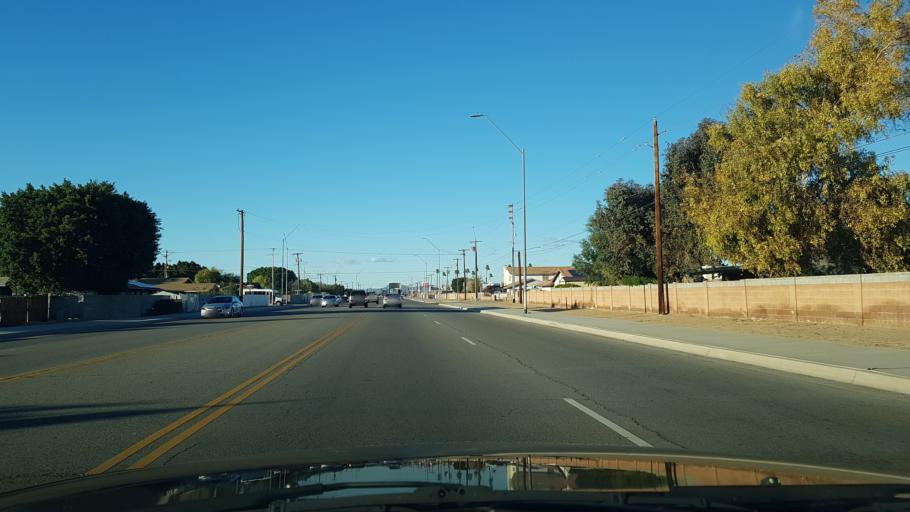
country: US
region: Arizona
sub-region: Yuma County
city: Yuma
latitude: 32.6788
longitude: -114.5988
